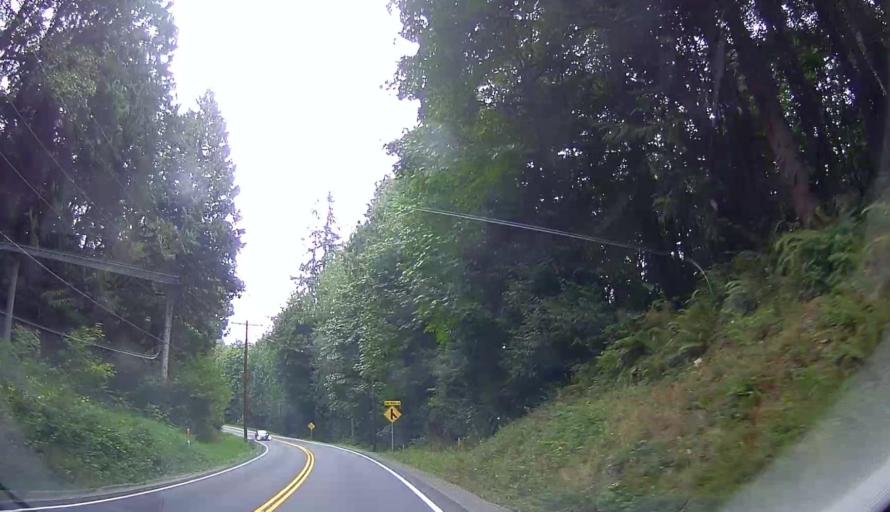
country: US
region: Washington
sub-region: Snohomish County
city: Warm Beach
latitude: 48.1872
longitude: -122.3417
